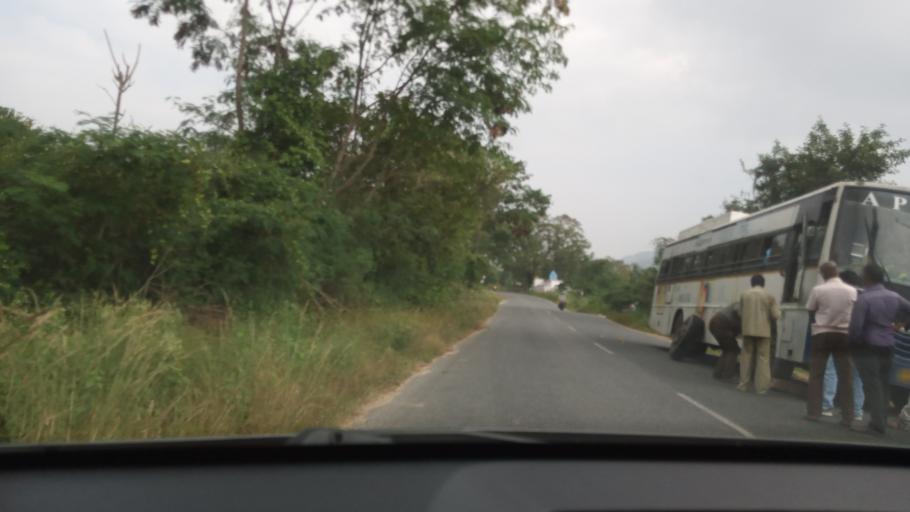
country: IN
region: Andhra Pradesh
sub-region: Chittoor
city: Pakala
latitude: 13.6562
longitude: 78.8539
